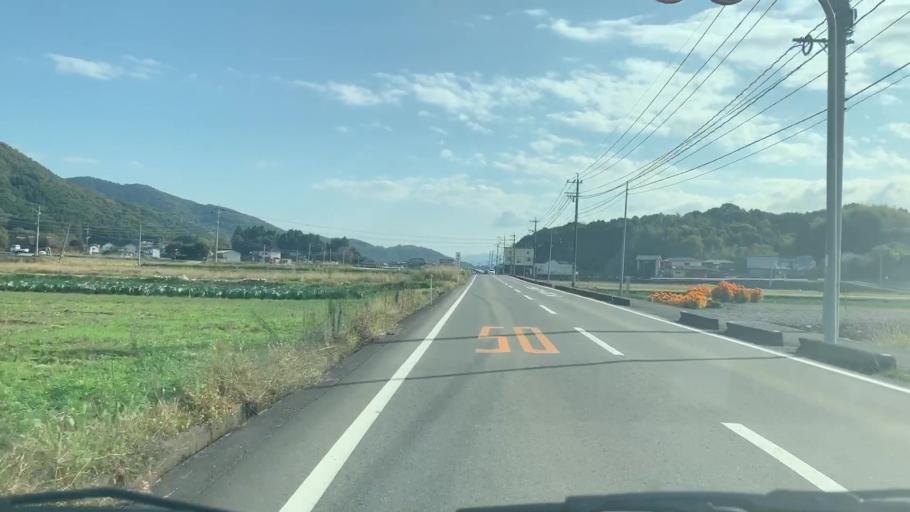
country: JP
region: Saga Prefecture
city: Takeocho-takeo
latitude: 33.1557
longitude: 130.0634
